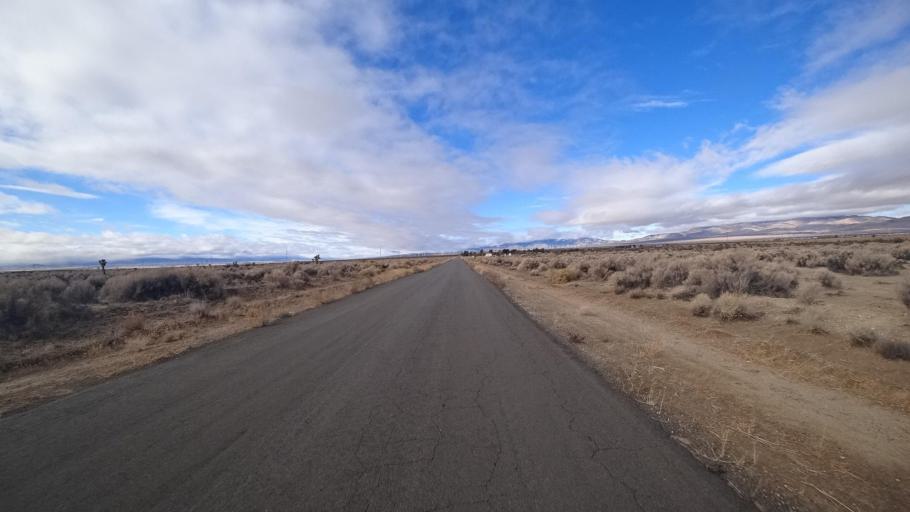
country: US
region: California
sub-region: Kern County
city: Rosamond
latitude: 34.8927
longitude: -118.2987
